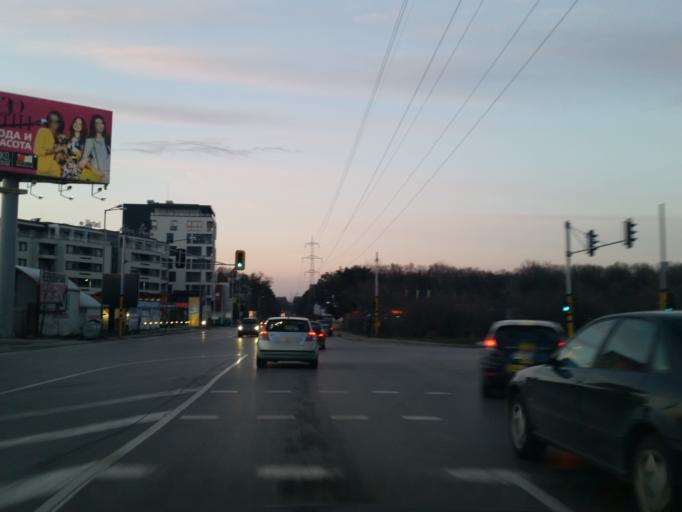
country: BG
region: Sofia-Capital
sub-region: Stolichna Obshtina
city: Sofia
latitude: 42.6574
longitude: 23.3365
